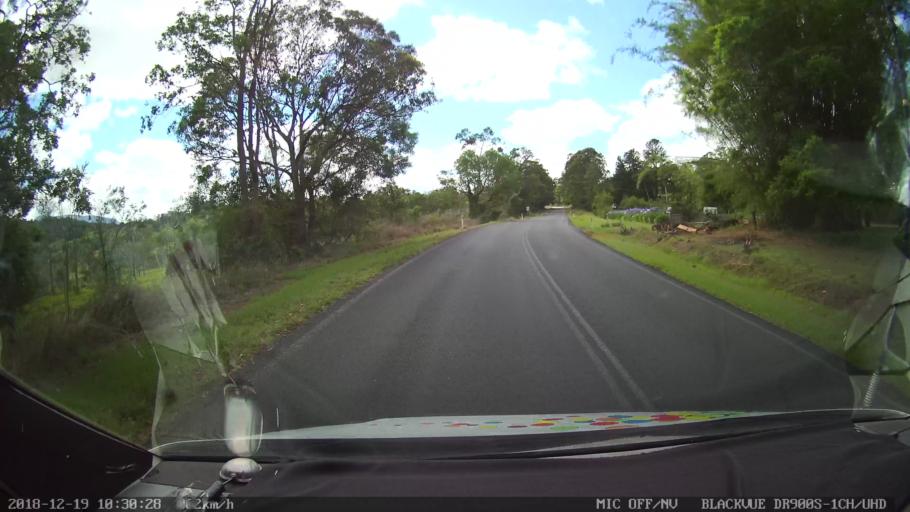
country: AU
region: New South Wales
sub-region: Lismore Municipality
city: Larnook
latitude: -28.5892
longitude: 153.1077
